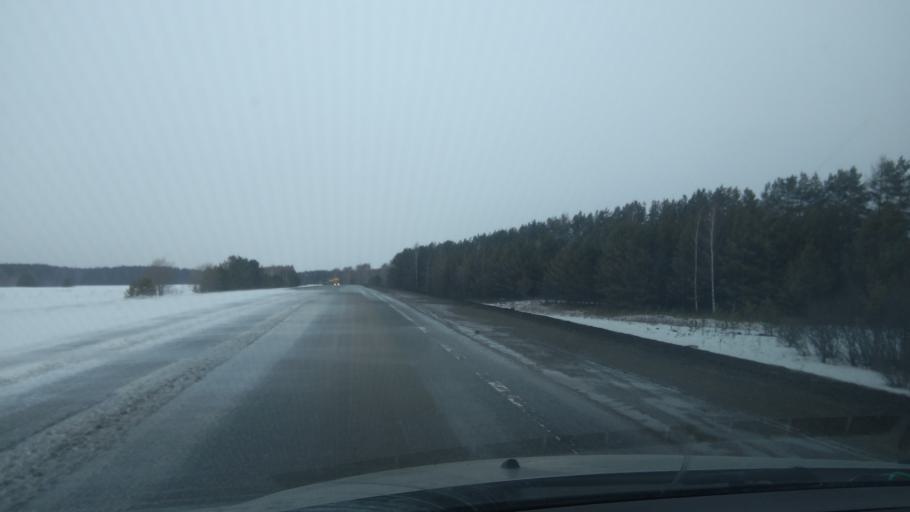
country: RU
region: Perm
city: Suksun
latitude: 56.9037
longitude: 57.5961
